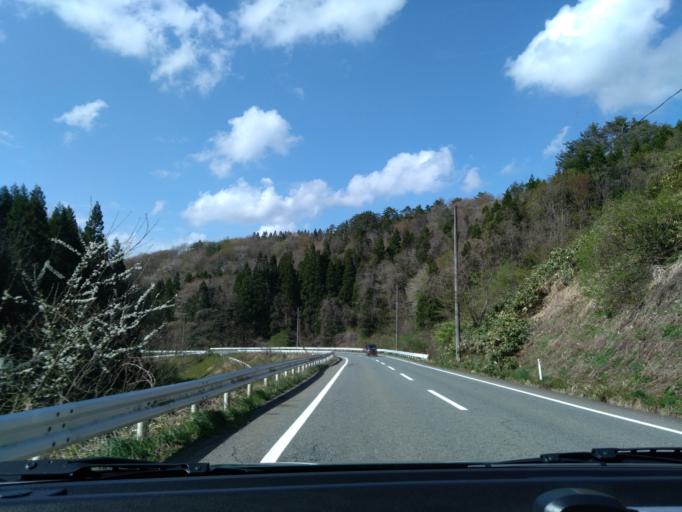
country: JP
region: Akita
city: Akita
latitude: 39.6971
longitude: 140.2211
